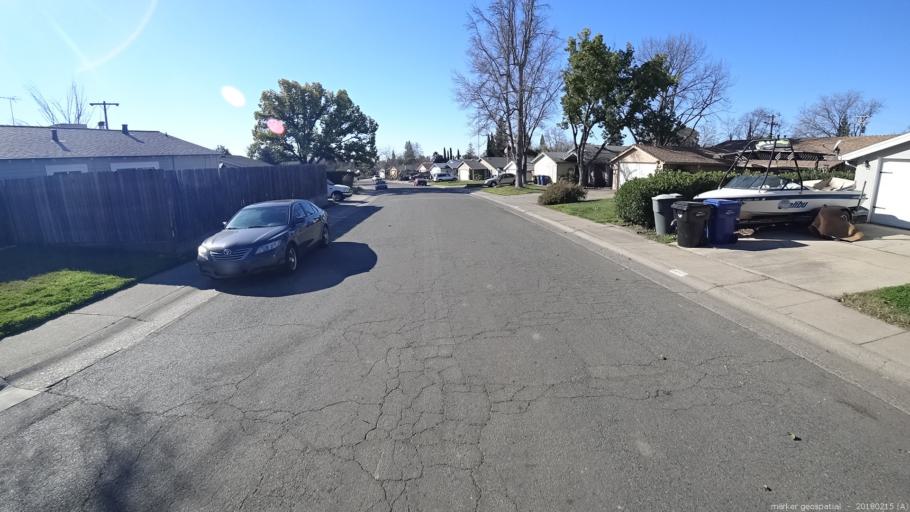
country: US
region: California
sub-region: Sacramento County
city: Foothill Farms
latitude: 38.6658
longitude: -121.3213
